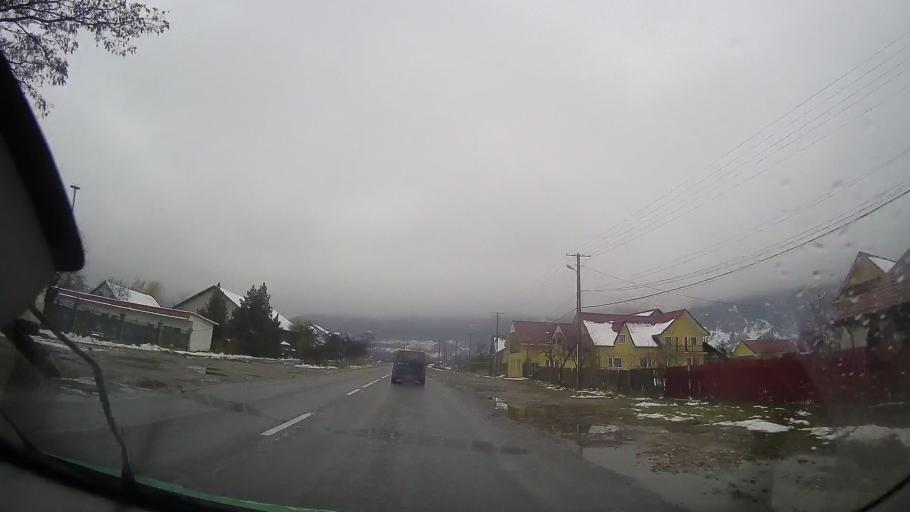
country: RO
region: Neamt
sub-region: Comuna Pangarati
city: Stejaru
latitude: 46.9116
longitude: 26.1807
